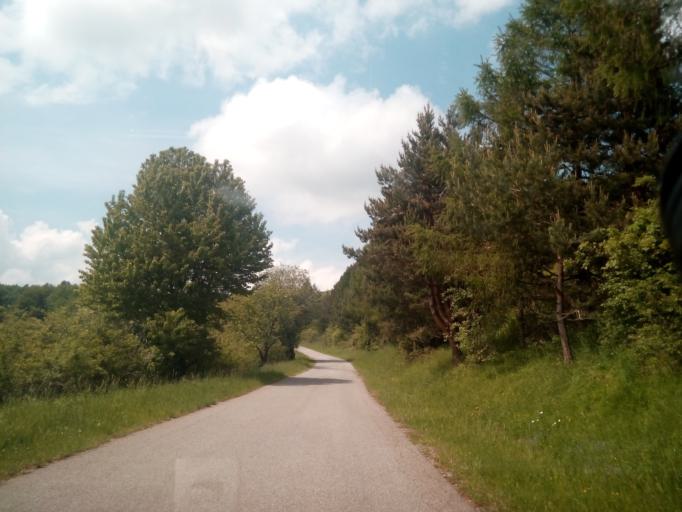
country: SK
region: Presovsky
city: Lipany
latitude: 49.0626
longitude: 20.9378
